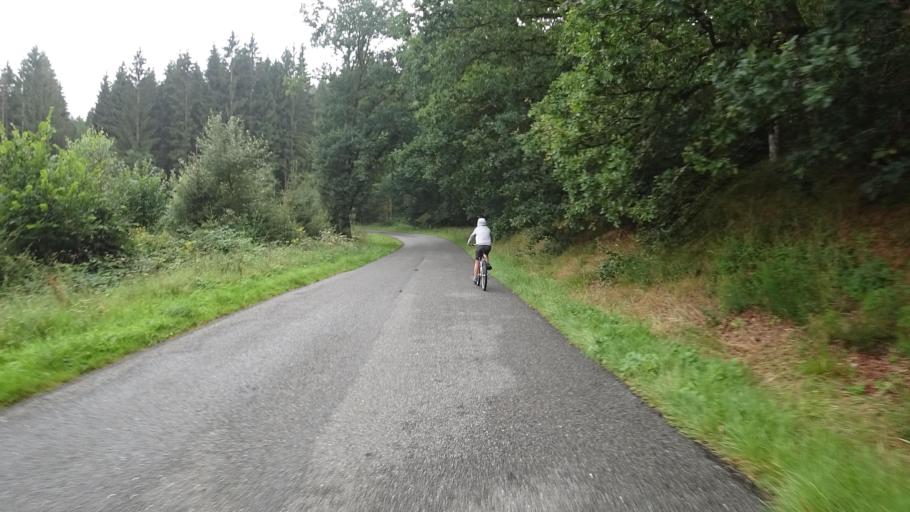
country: BE
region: Wallonia
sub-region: Province du Luxembourg
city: Chiny
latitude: 49.7882
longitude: 5.3735
